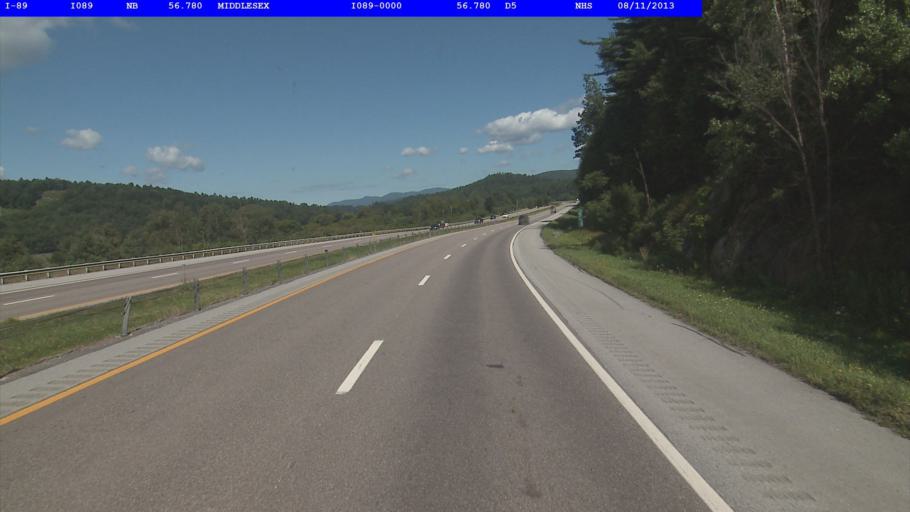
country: US
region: Vermont
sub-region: Washington County
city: Montpelier
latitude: 44.2797
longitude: -72.6582
